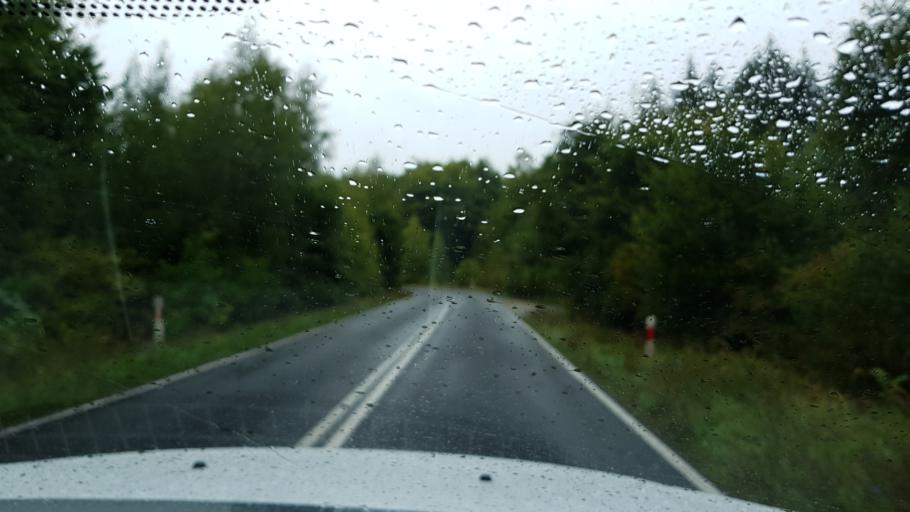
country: PL
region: West Pomeranian Voivodeship
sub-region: Powiat gryfinski
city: Widuchowa
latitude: 53.0869
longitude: 14.4020
